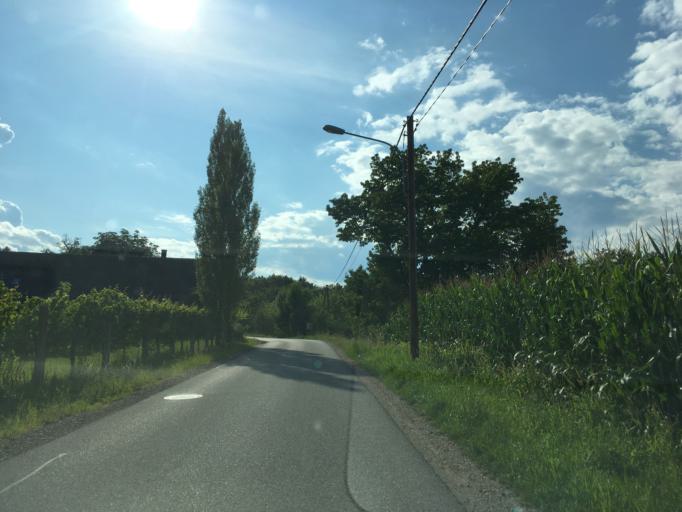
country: AT
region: Styria
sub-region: Politischer Bezirk Leibnitz
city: Sankt Nikolai im Sausal
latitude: 46.8058
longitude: 15.4471
